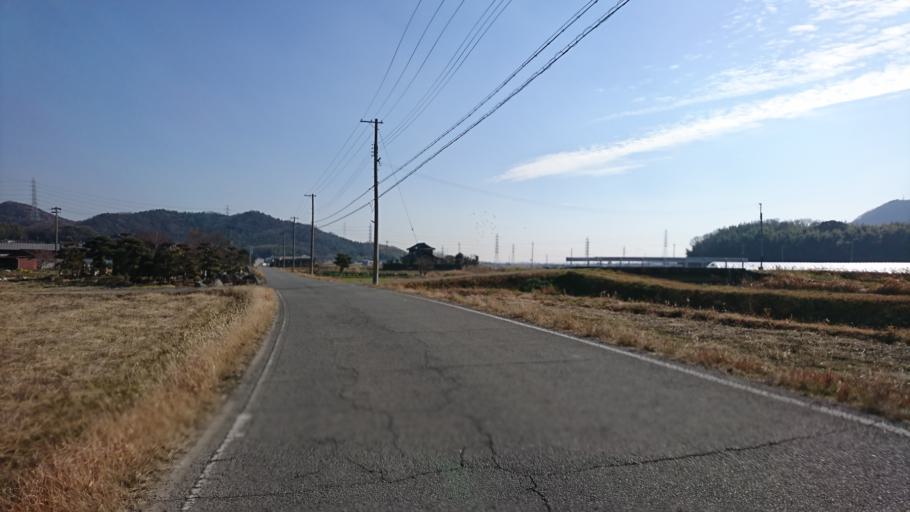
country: JP
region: Hyogo
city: Kakogawacho-honmachi
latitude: 34.8219
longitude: 134.8463
